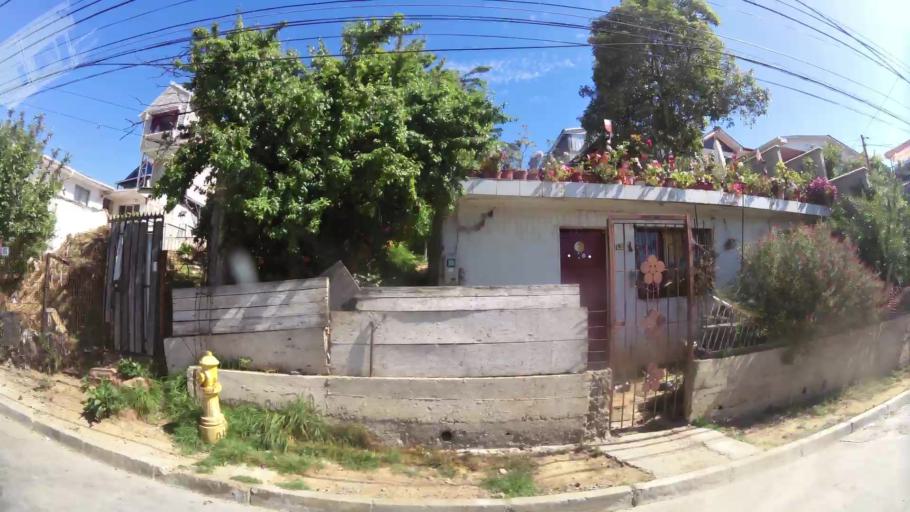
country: CL
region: Valparaiso
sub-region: Provincia de Valparaiso
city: Vina del Mar
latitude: -33.0407
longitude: -71.5678
